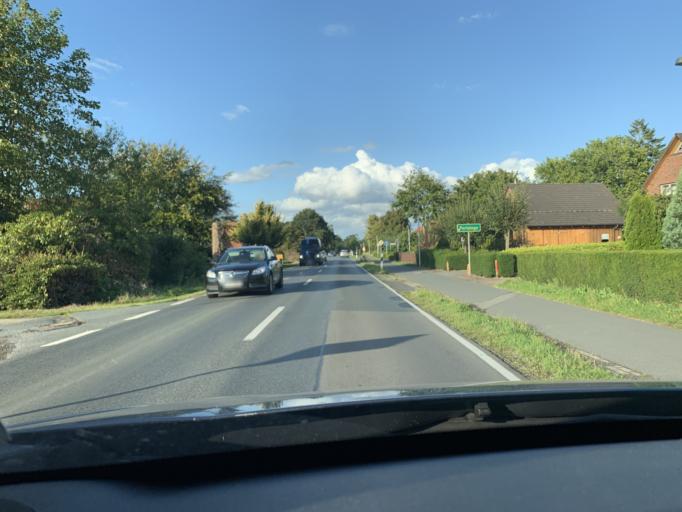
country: DE
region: Lower Saxony
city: Edewecht
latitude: 53.1416
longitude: 7.9924
